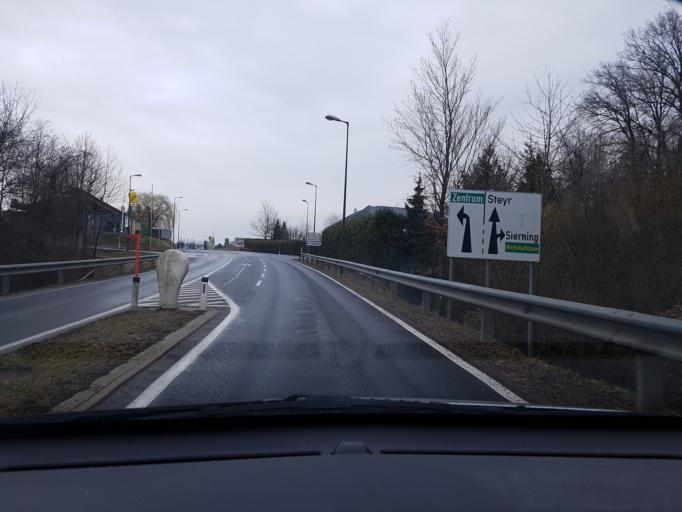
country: AT
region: Upper Austria
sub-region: Steyr Stadt
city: Steyr
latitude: 48.0794
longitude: 14.3731
